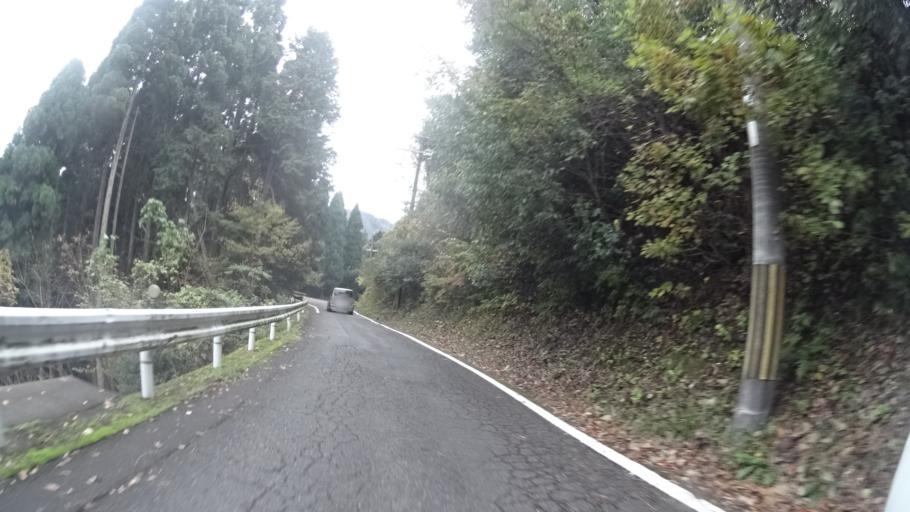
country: JP
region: Kyoto
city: Maizuru
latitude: 35.4933
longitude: 135.4649
